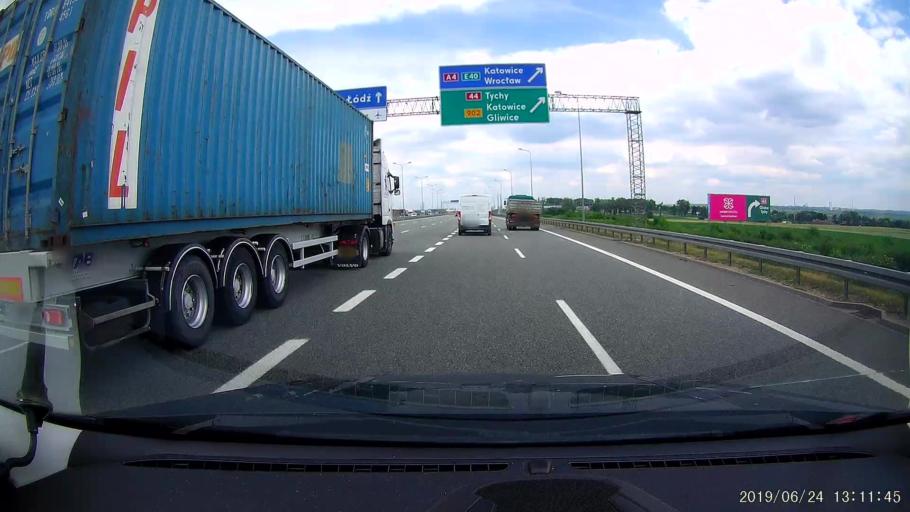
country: PL
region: Silesian Voivodeship
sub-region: Powiat gliwicki
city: Gieraltowice
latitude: 50.2488
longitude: 18.7151
